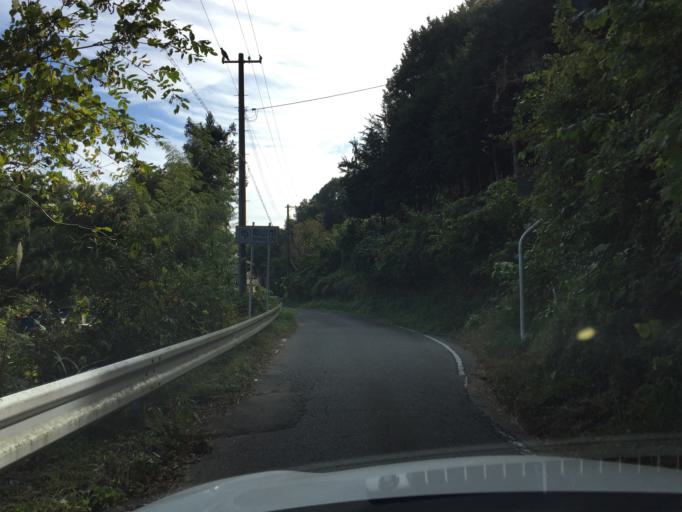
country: JP
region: Fukushima
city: Miharu
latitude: 37.3858
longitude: 140.4531
